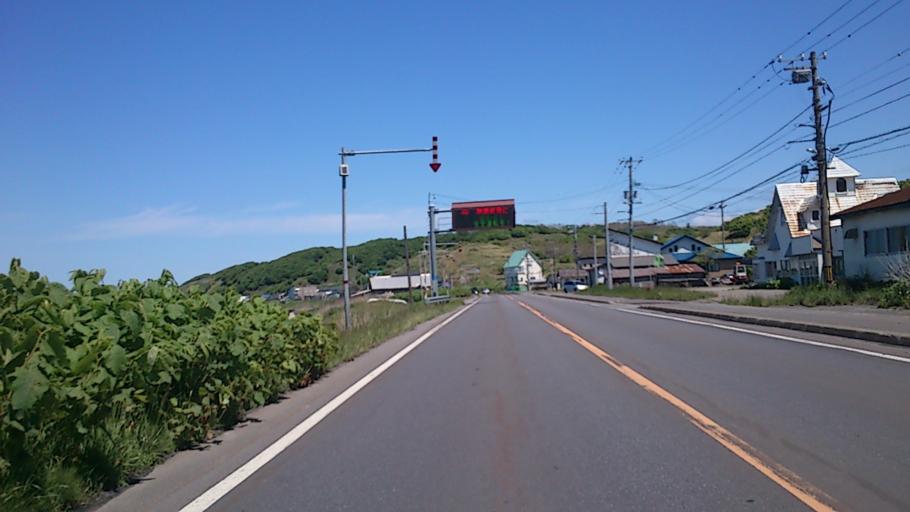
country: JP
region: Hokkaido
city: Rumoi
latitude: 43.9638
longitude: 141.6437
